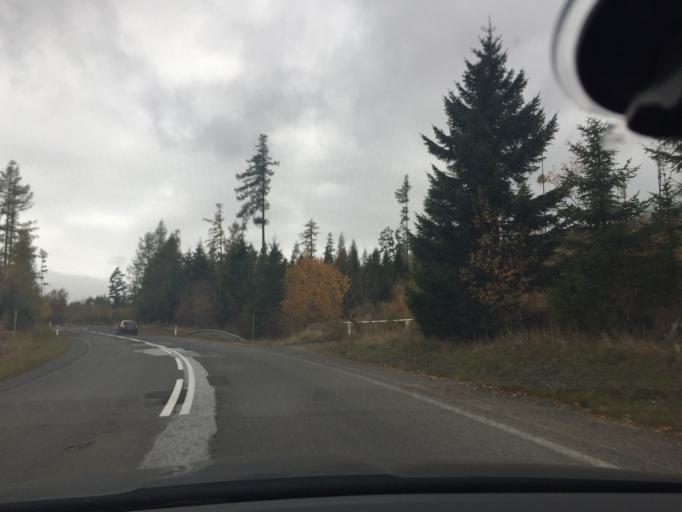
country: SK
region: Presovsky
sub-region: Okres Poprad
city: Strba
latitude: 49.1183
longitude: 20.1364
